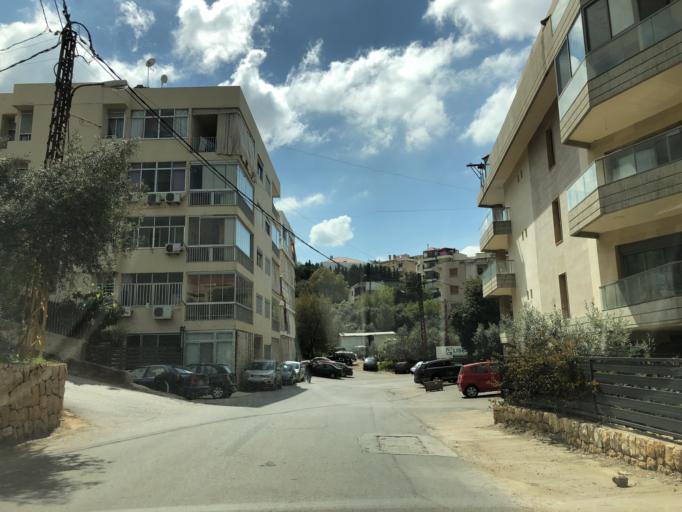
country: LB
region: Mont-Liban
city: Baabda
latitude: 33.8542
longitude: 35.5746
